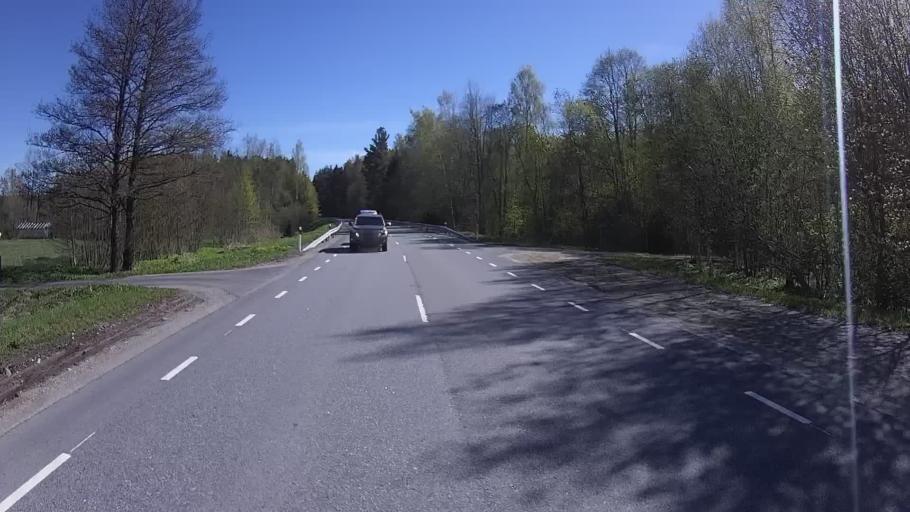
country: EE
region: Harju
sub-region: Loksa linn
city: Loksa
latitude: 59.5594
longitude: 25.7244
